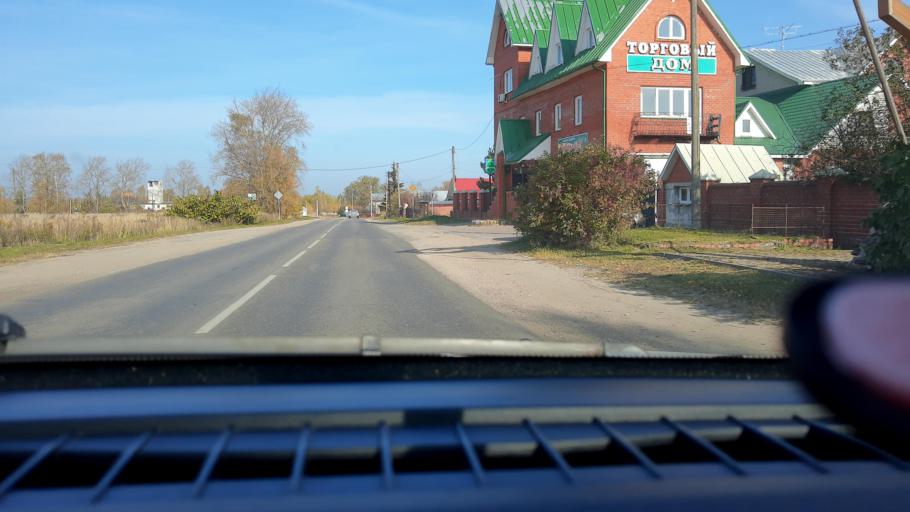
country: RU
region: Nizjnij Novgorod
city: Kstovo
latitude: 56.1503
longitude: 44.2316
